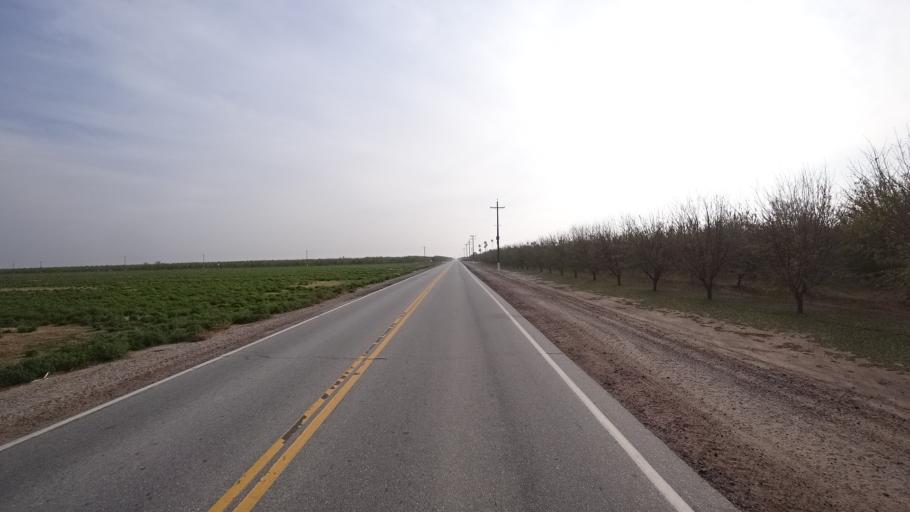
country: US
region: California
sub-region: Kern County
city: Greenacres
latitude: 35.2835
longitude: -119.1283
